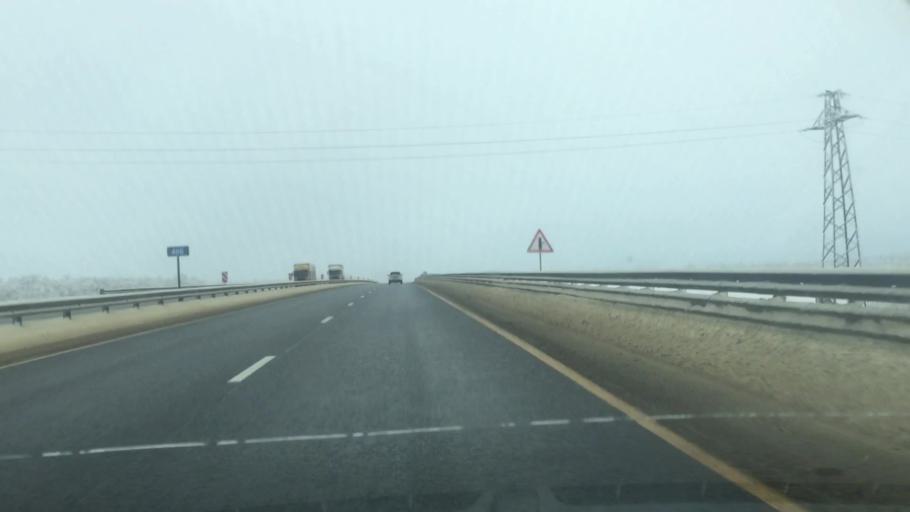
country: RU
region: Lipetsk
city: Zadonsk
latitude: 52.5059
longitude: 38.7556
